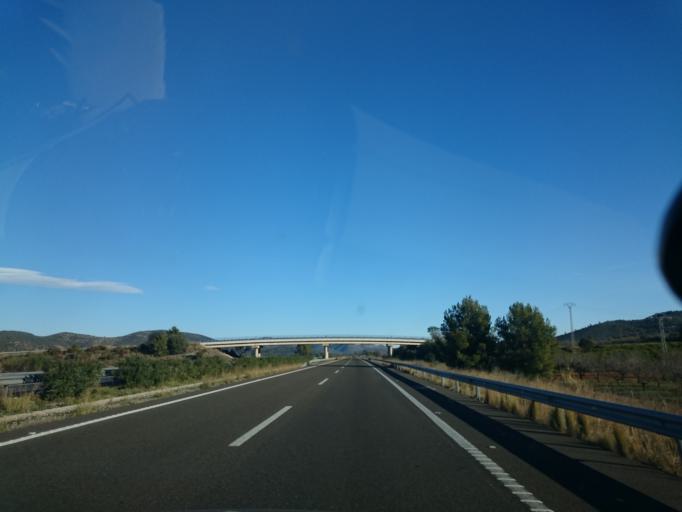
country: ES
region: Valencia
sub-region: Provincia de Castello
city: Alcala de Xivert
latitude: 40.3204
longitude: 0.2518
